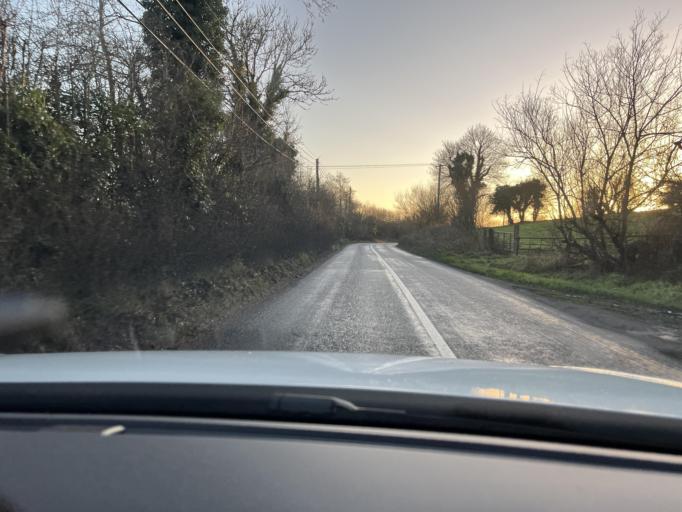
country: IE
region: Ulster
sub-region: An Cabhan
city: Ballyconnell
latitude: 54.1122
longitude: -7.5870
